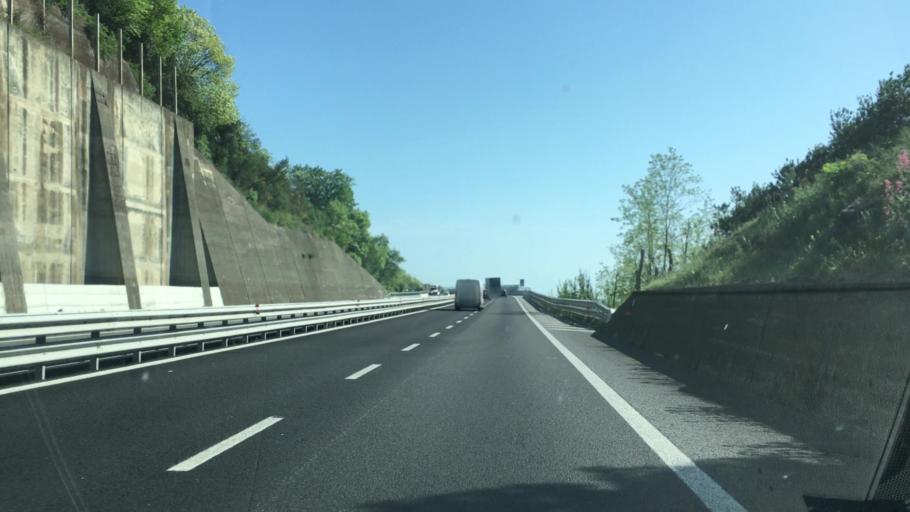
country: IT
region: Liguria
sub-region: Provincia di Genova
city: Cogorno
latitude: 44.2984
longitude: 9.3839
